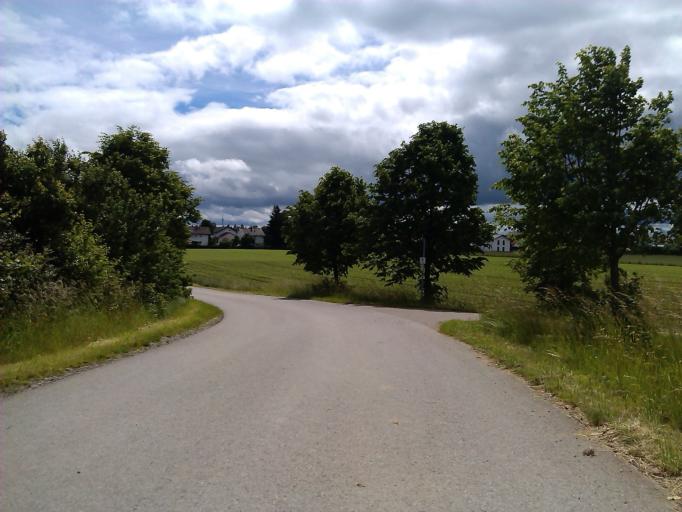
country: DE
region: Bavaria
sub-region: Swabia
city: Bad Worishofen
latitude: 47.9729
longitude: 10.6152
